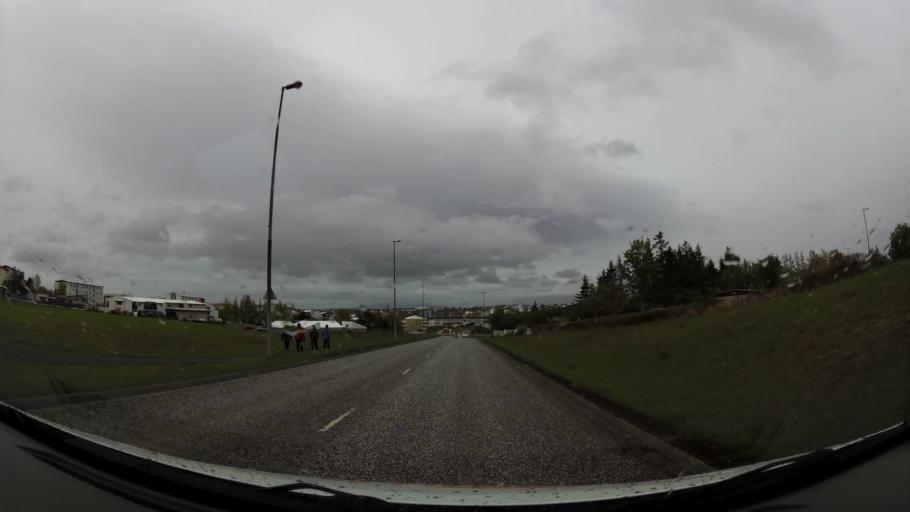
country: IS
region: Capital Region
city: Hafnarfjoerdur
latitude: 64.0583
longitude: -21.9647
